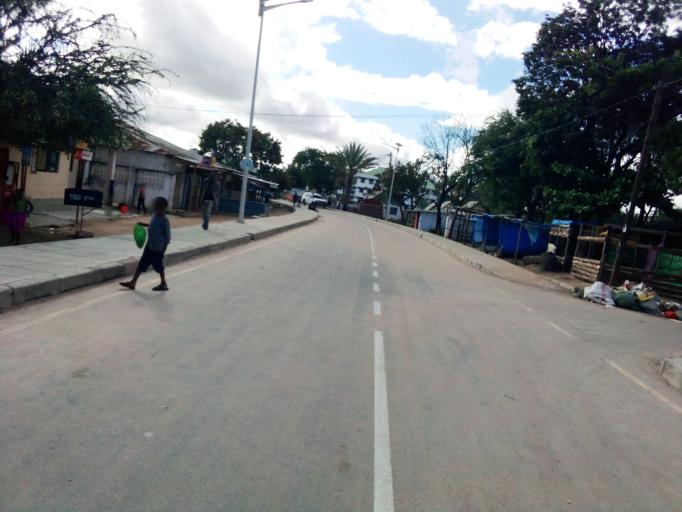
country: TZ
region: Dodoma
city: Dodoma
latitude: -6.1808
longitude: 35.7403
